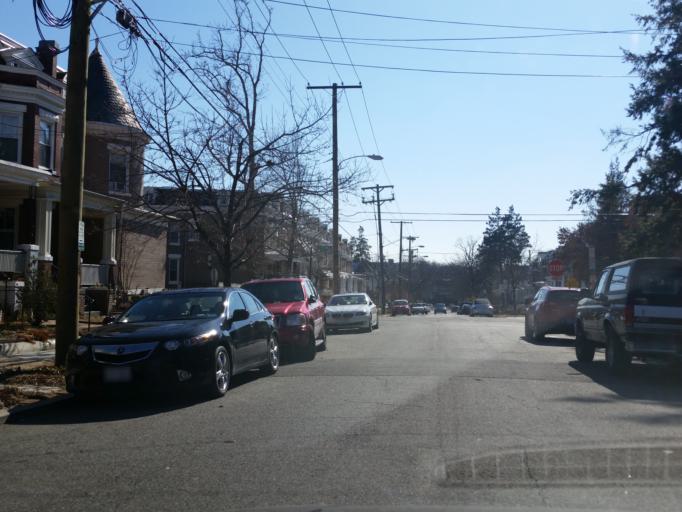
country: US
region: Maryland
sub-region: Montgomery County
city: Takoma Park
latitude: 38.9455
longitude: -77.0345
